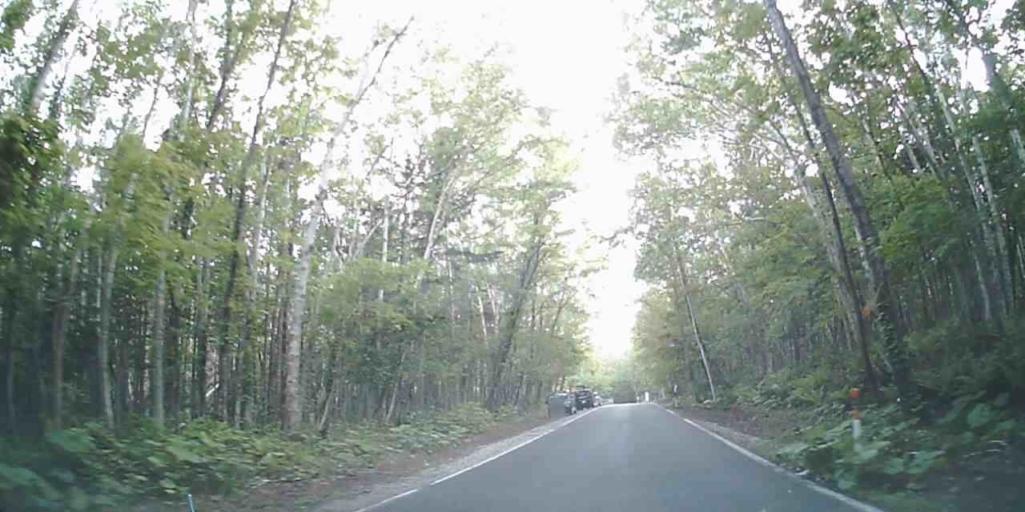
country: JP
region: Hokkaido
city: Shiraoi
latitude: 42.7180
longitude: 141.4091
